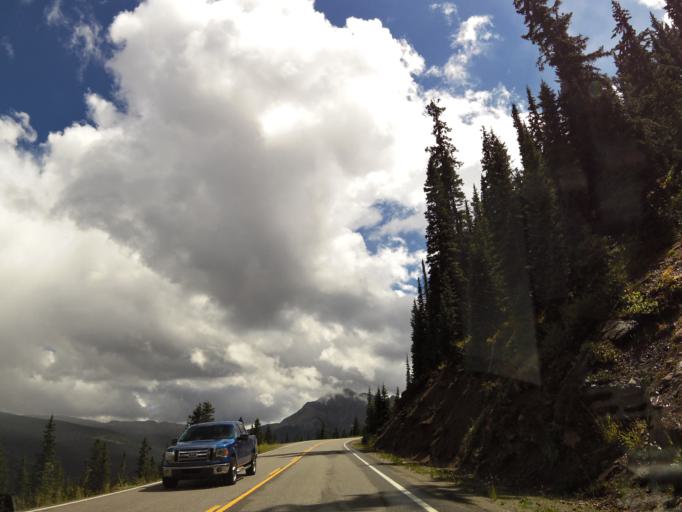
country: US
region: Colorado
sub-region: San Juan County
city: Silverton
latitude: 37.7066
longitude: -107.7703
